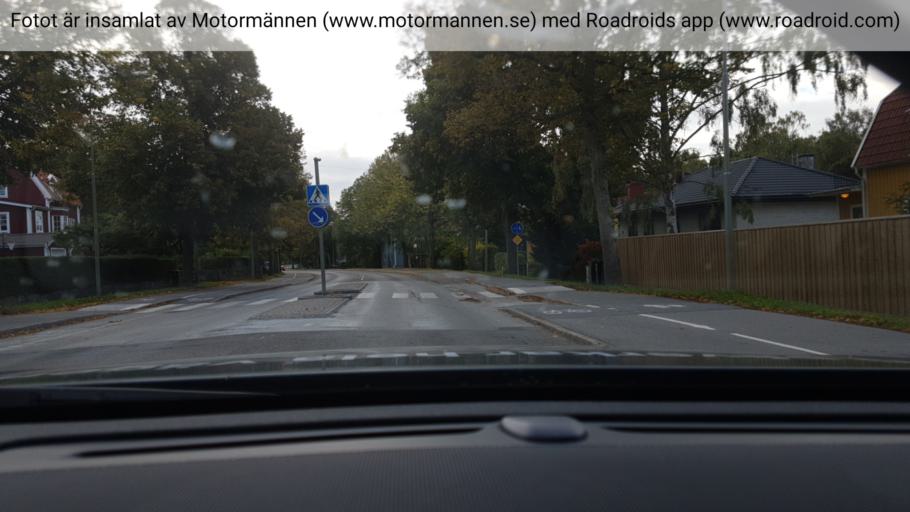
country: SE
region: Stockholm
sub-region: Stockholms Kommun
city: Bromma
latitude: 59.3505
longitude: 17.9204
